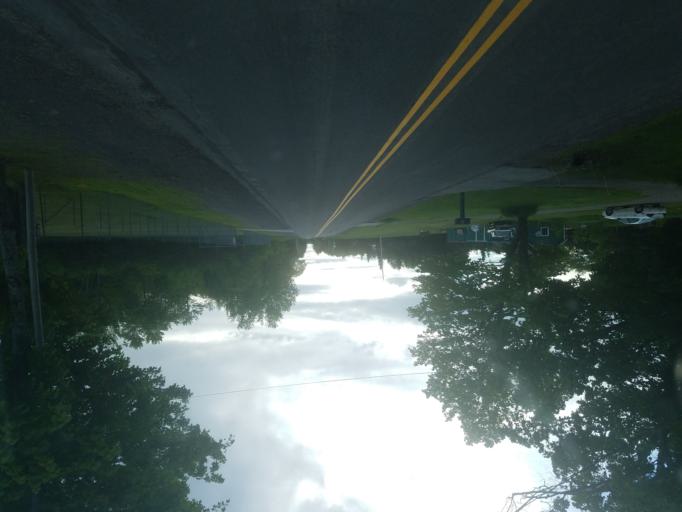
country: US
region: New York
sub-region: Herkimer County
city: Dolgeville
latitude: 43.3120
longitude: -74.9642
